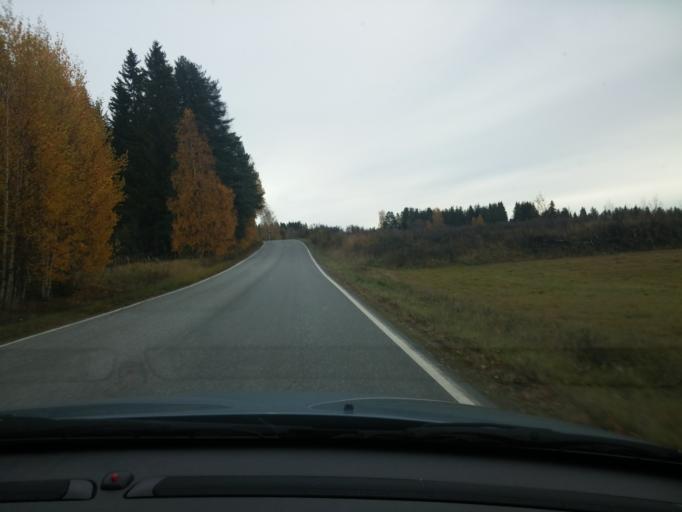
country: FI
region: Haeme
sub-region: Forssa
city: Tammela
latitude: 60.7653
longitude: 23.8619
